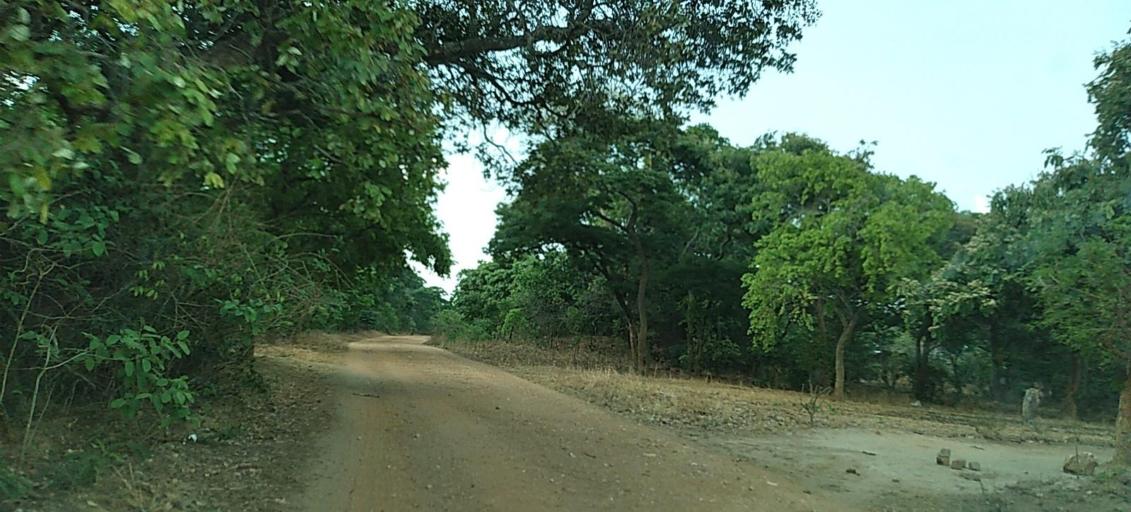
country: ZM
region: Copperbelt
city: Mpongwe
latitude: -13.4853
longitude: 28.0841
